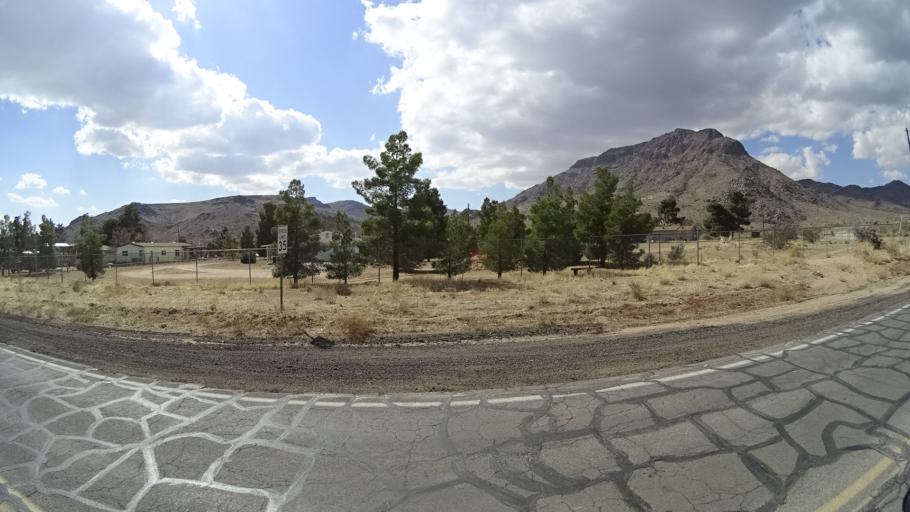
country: US
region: Arizona
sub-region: Mohave County
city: New Kingman-Butler
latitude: 35.2730
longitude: -114.0461
